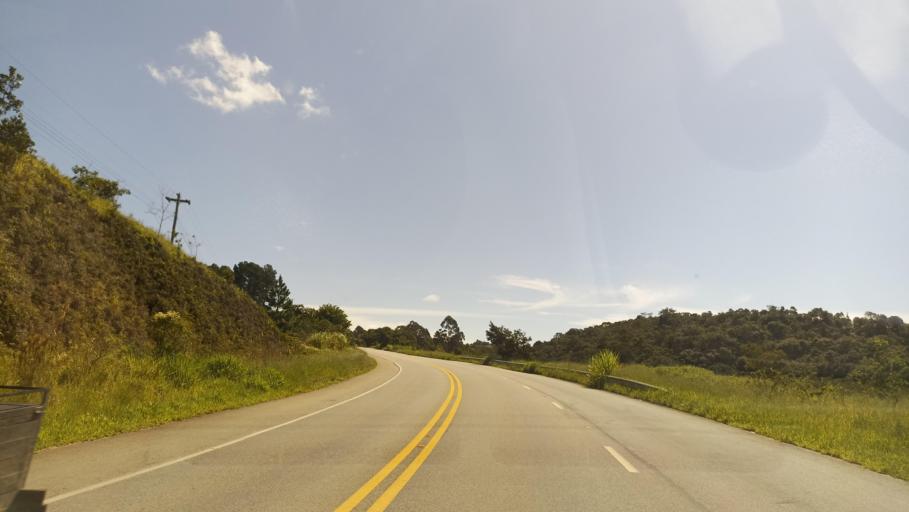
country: BR
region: Sao Paulo
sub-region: Guaratingueta
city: Guaratingueta
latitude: -22.9351
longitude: -45.0710
